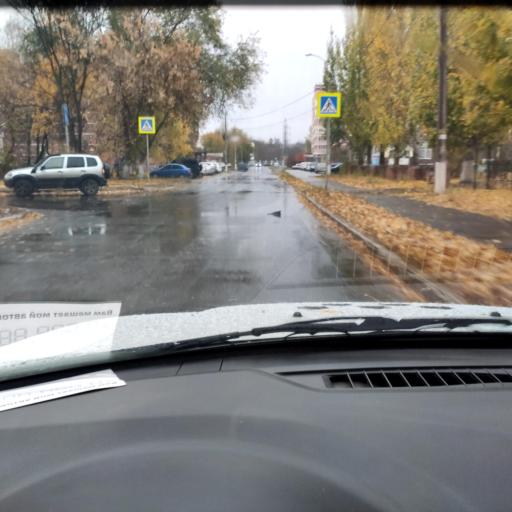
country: RU
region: Samara
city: Tol'yatti
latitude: 53.5036
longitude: 49.4232
